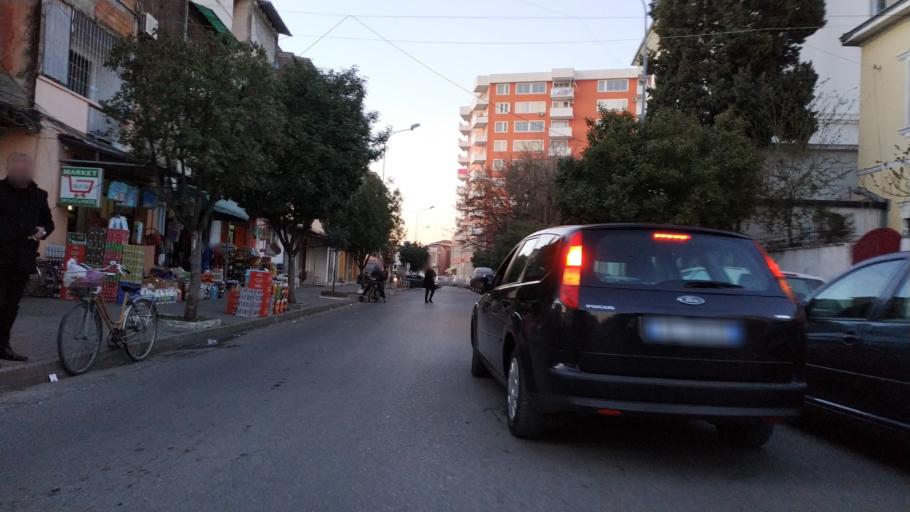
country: AL
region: Shkoder
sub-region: Rrethi i Shkodres
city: Shkoder
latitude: 42.0747
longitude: 19.5187
